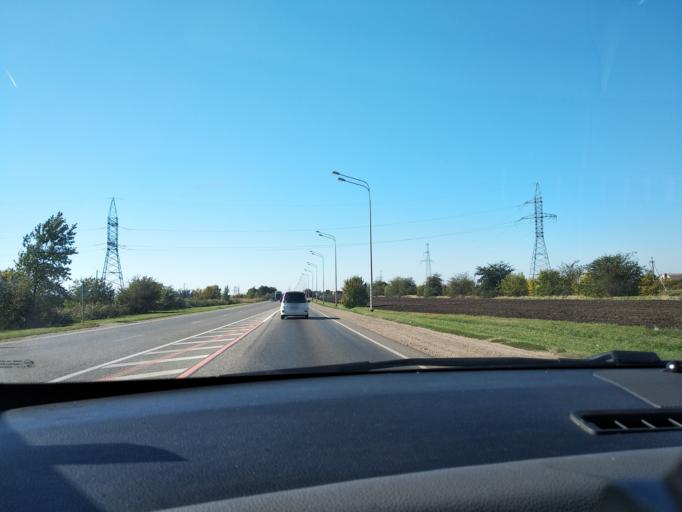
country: RU
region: Krasnodarskiy
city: Agronom
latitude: 45.1718
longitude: 39.0965
